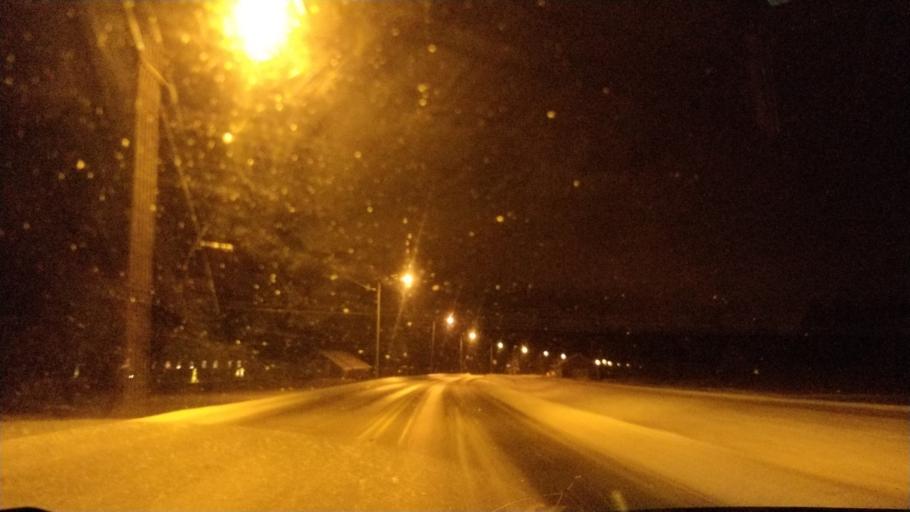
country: FI
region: Lapland
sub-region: Rovaniemi
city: Rovaniemi
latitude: 66.3178
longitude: 25.3608
